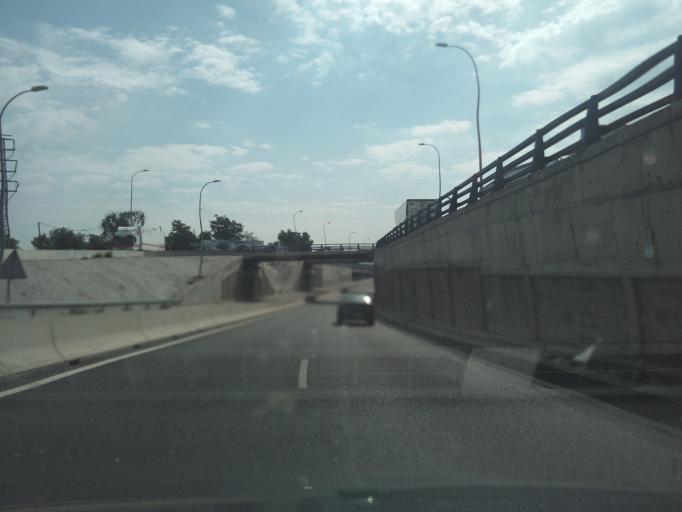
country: ES
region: Madrid
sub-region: Provincia de Madrid
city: San Fernando de Henares
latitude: 40.4446
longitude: -3.5347
